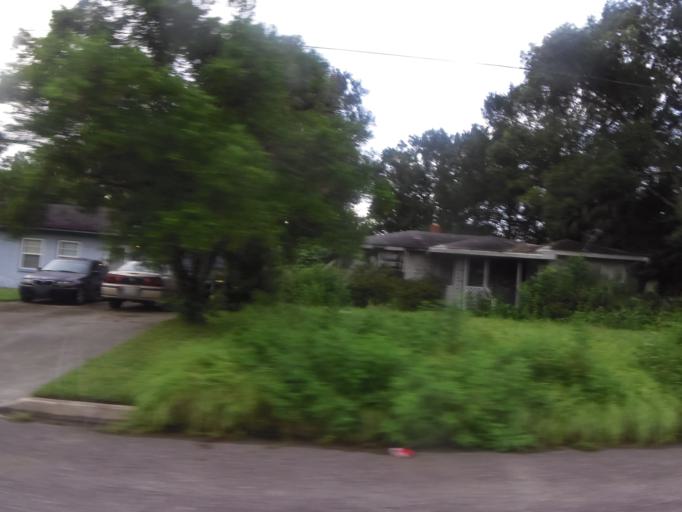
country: US
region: Florida
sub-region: Duval County
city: Jacksonville
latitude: 30.3515
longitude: -81.7199
